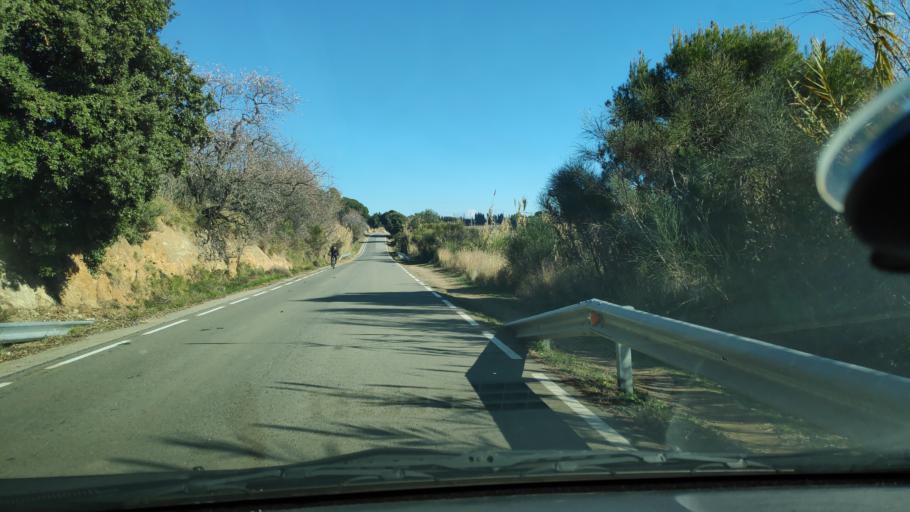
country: ES
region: Catalonia
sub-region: Provincia de Barcelona
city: Matadepera
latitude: 41.5951
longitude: 2.0107
